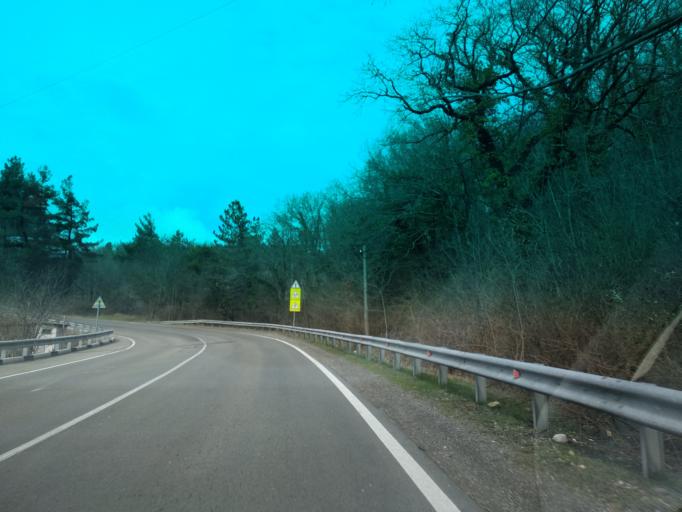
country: RU
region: Krasnodarskiy
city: Shepsi
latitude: 44.0443
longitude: 39.1426
